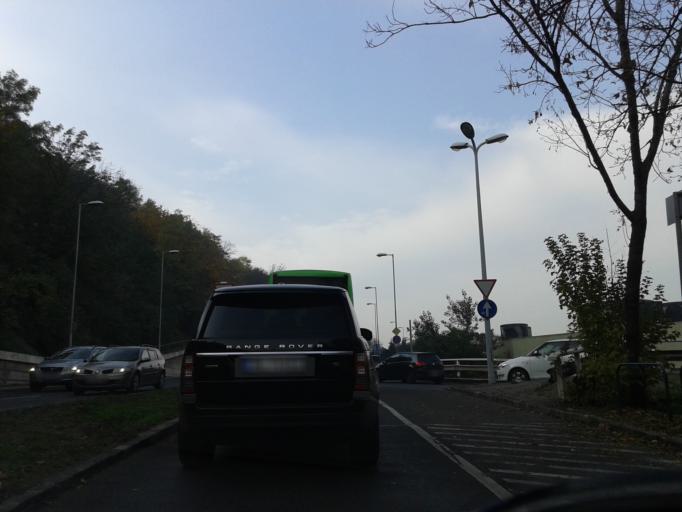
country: HU
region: Budapest
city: Budapest I. keruelet
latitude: 47.4903
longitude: 19.0444
